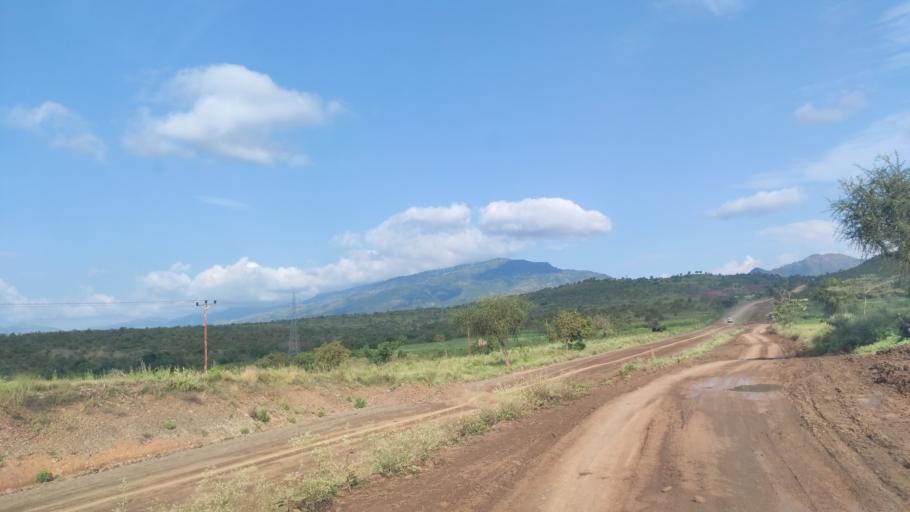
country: ET
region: Southern Nations, Nationalities, and People's Region
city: Felege Neway
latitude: 6.4349
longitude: 37.2821
